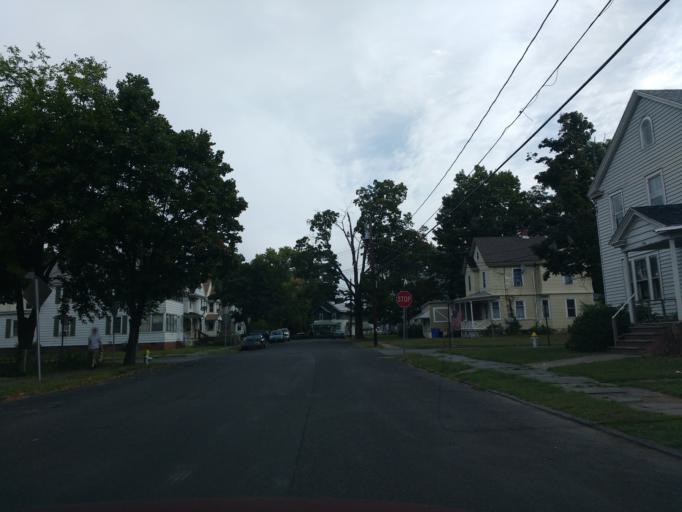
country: US
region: New York
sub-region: Ulster County
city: Kingston
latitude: 41.9368
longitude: -74.0004
